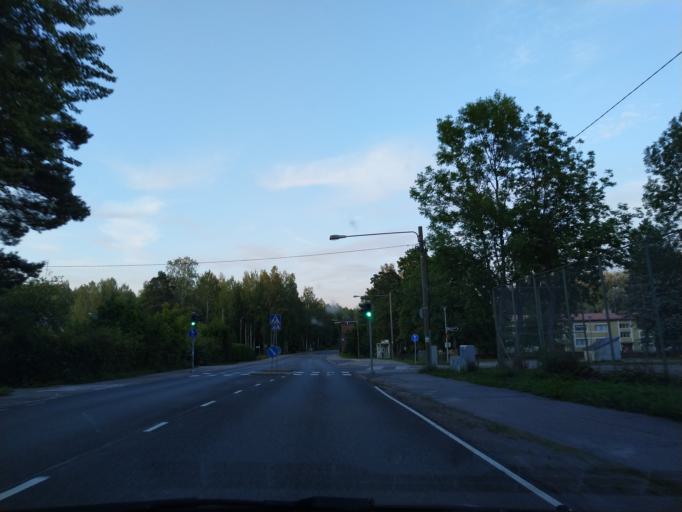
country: FI
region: Uusimaa
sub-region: Helsinki
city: Tuusula
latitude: 60.3567
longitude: 25.0540
